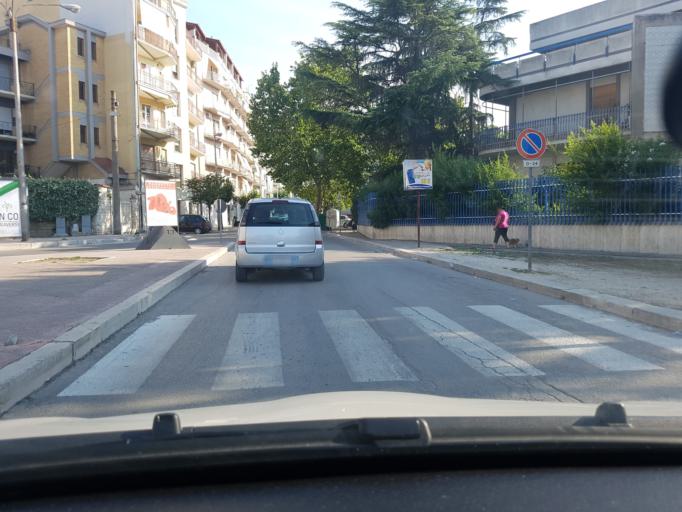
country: IT
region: Apulia
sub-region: Provincia di Foggia
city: Cerignola
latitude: 41.2654
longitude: 15.9086
